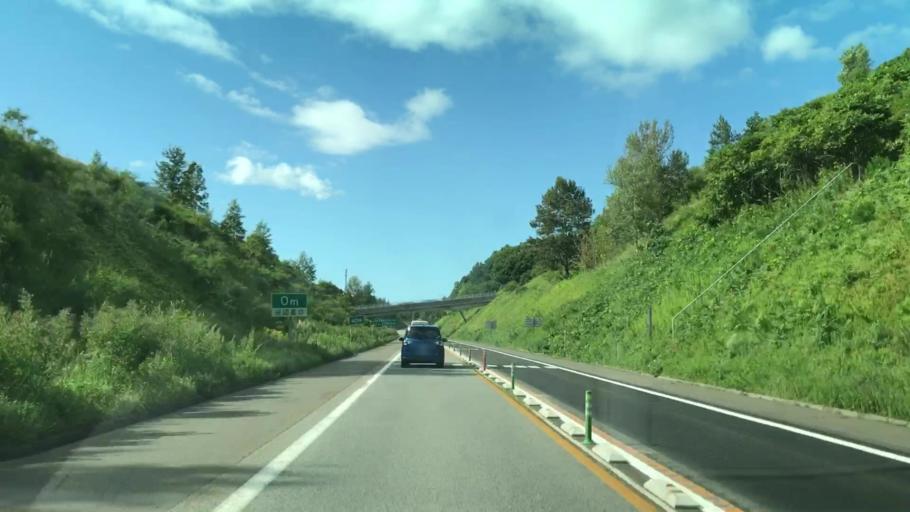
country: JP
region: Hokkaido
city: Date
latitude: 42.4373
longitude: 140.9205
